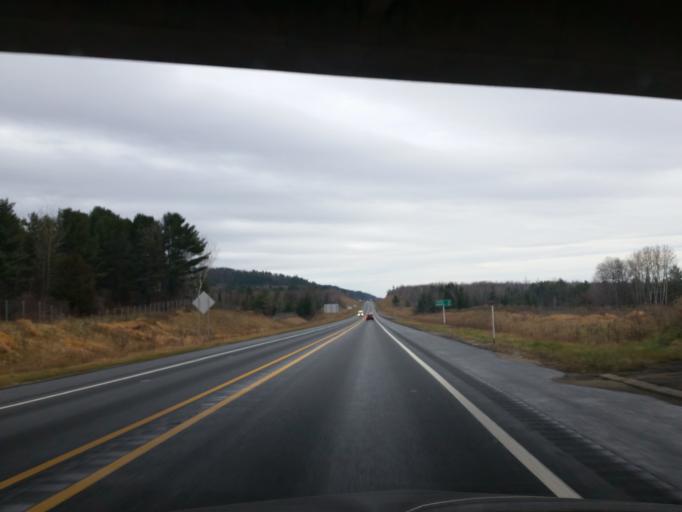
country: CA
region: Quebec
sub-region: Outaouais
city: Papineauville
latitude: 45.6709
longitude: -74.9169
